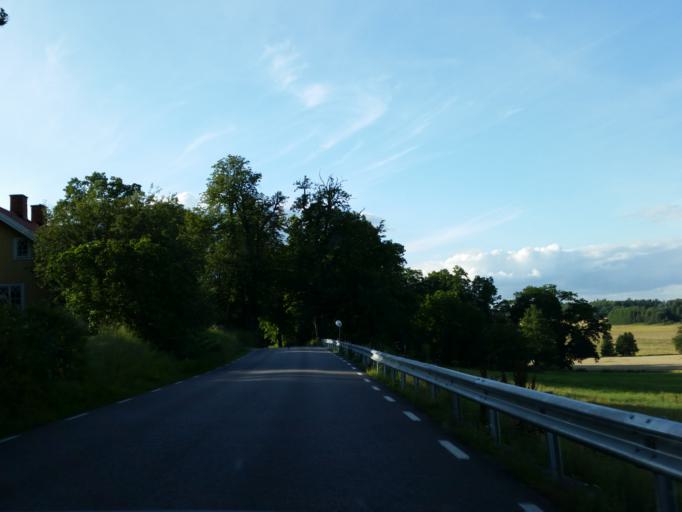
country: SE
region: Stockholm
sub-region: Sodertalje Kommun
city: Molnbo
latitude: 59.0160
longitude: 17.3665
